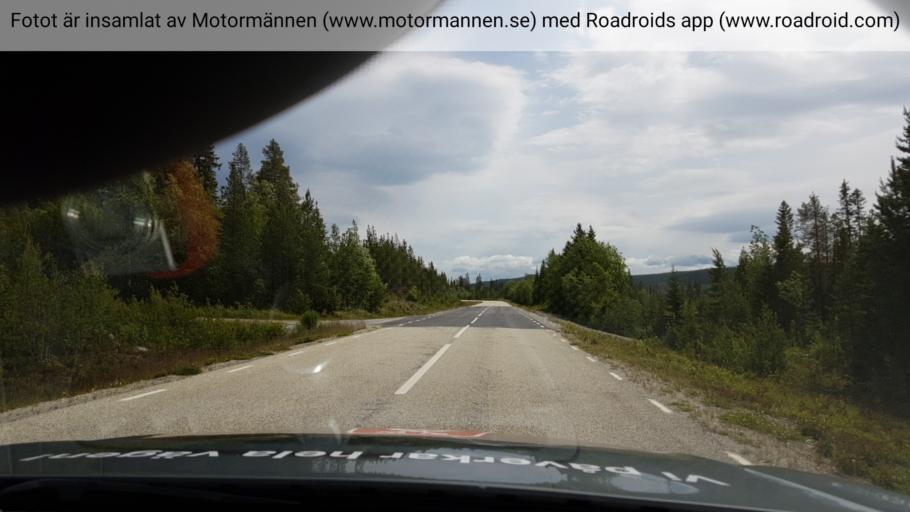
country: SE
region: Jaemtland
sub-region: Are Kommun
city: Jarpen
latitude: 62.8137
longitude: 13.5207
